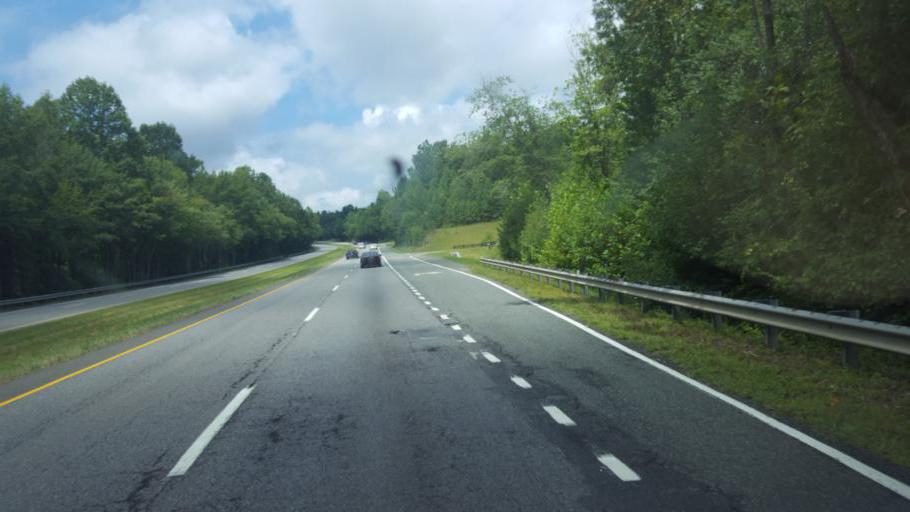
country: US
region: Virginia
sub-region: Stafford County
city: Falmouth
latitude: 38.4128
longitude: -77.6051
